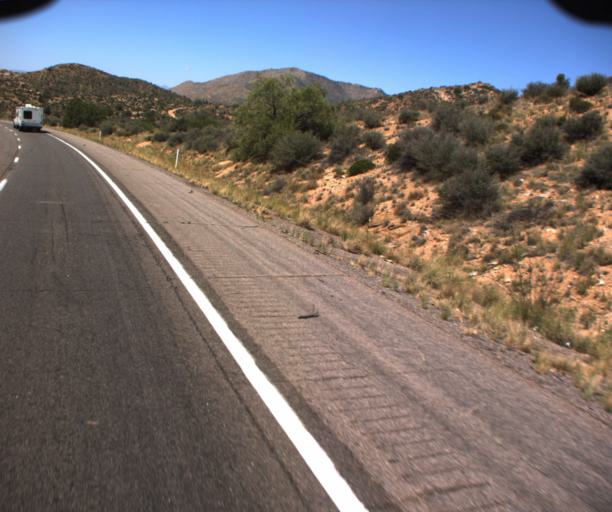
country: US
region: Arizona
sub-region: Mohave County
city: Peach Springs
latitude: 35.1788
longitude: -113.4945
